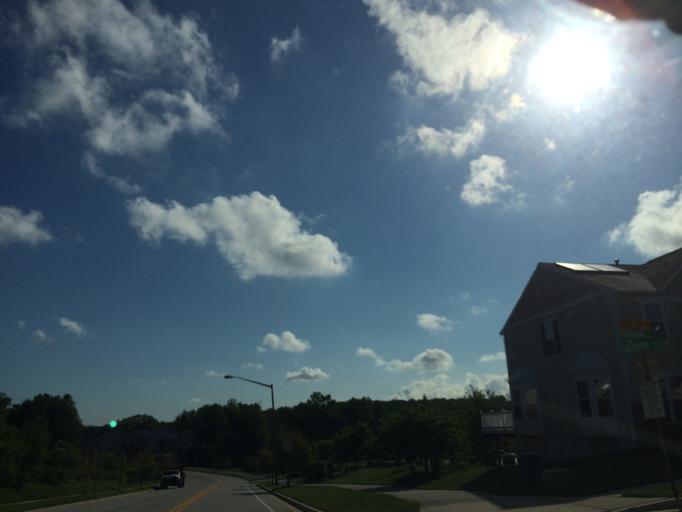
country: US
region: Maryland
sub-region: Howard County
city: Hanover
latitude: 39.1575
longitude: -76.7374
